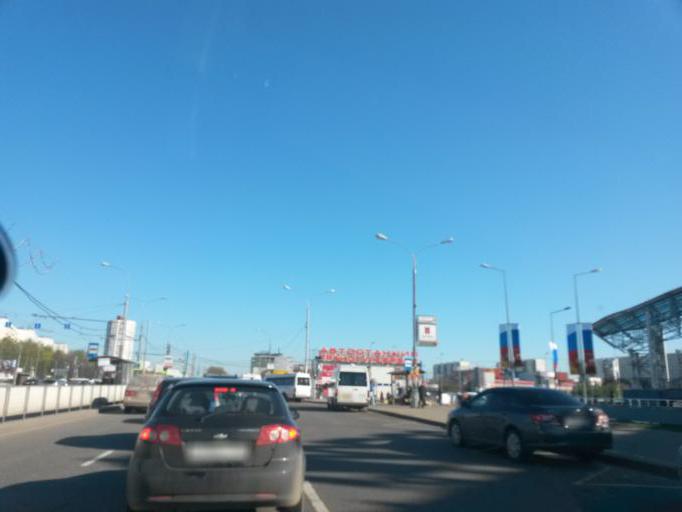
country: RU
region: Moscow
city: Orekhovo-Borisovo
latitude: 55.6094
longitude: 37.7187
